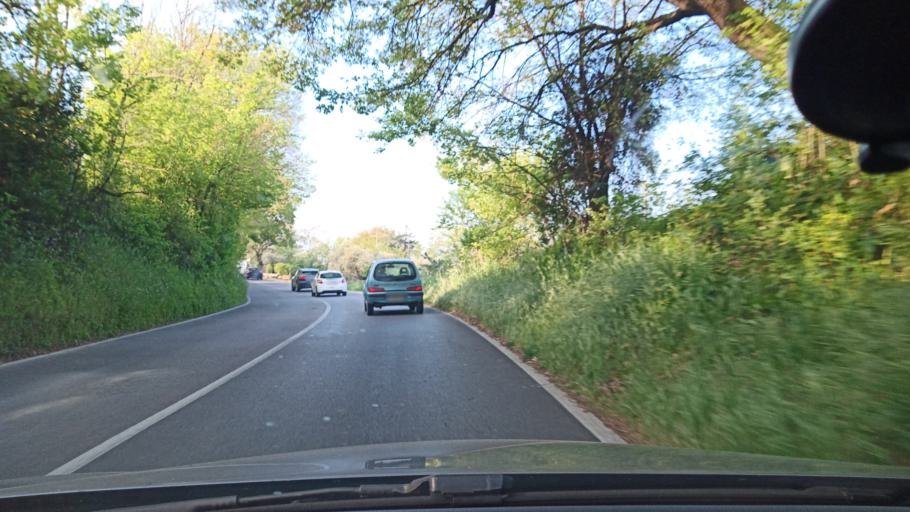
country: IT
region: Latium
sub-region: Citta metropolitana di Roma Capitale
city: Fiano Romano
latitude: 42.1841
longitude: 12.6368
